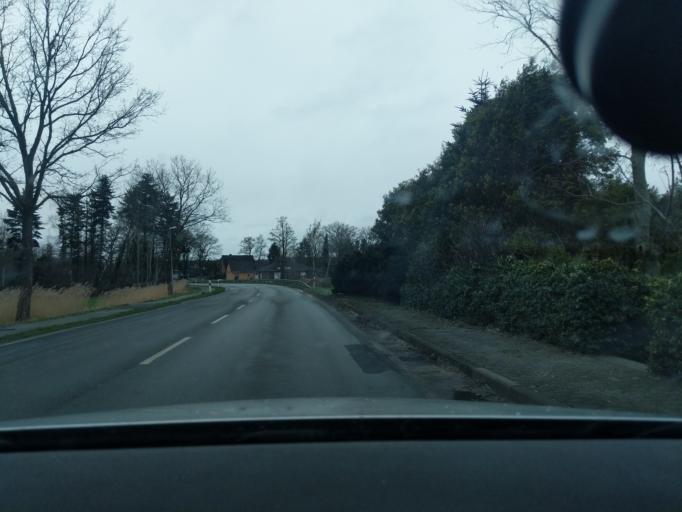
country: DE
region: Lower Saxony
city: Kutenholz
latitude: 53.4865
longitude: 9.3231
